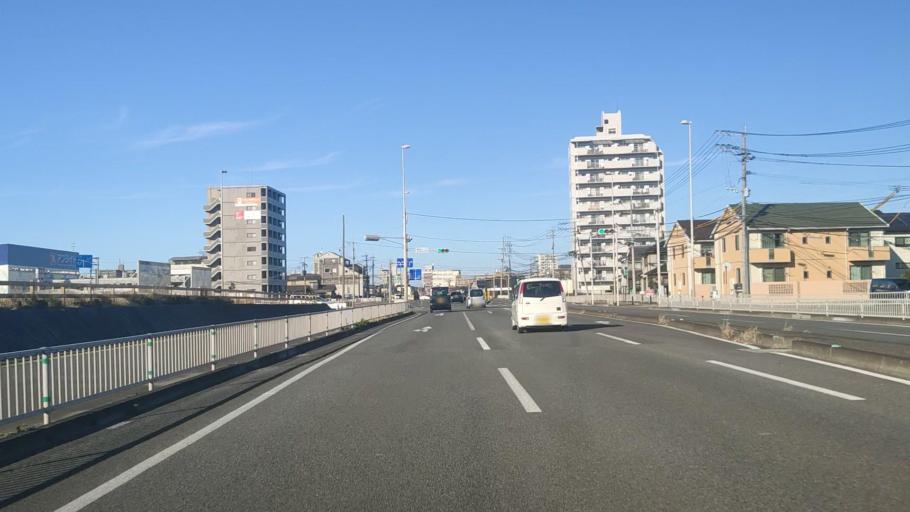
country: JP
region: Oita
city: Oita
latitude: 33.2295
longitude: 131.6188
